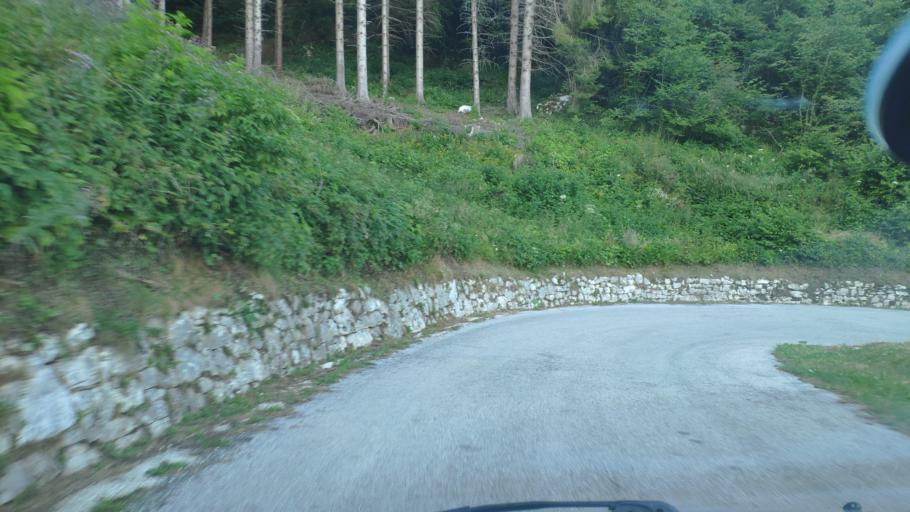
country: IT
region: Veneto
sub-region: Provincia di Vicenza
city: Calvene
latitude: 45.7907
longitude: 11.5199
